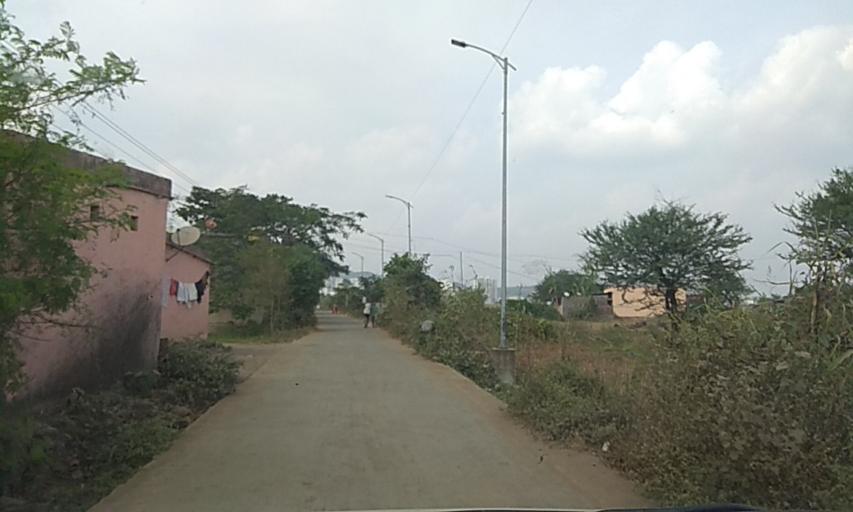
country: IN
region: Maharashtra
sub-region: Pune Division
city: Pimpri
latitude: 18.5782
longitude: 73.7084
